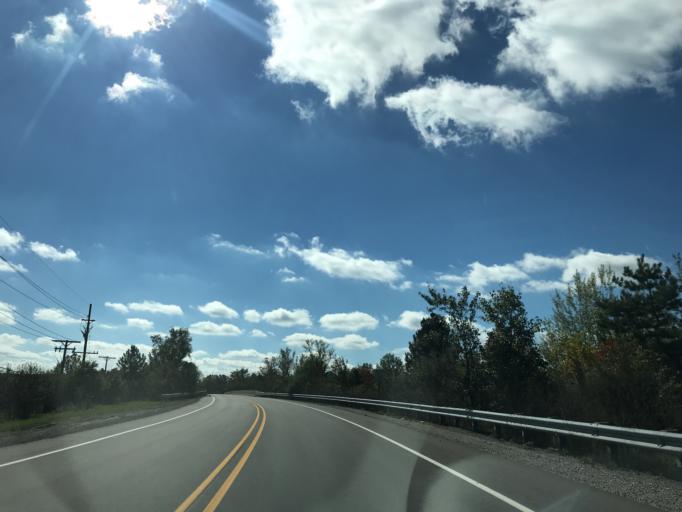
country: US
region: Michigan
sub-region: Washtenaw County
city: Ann Arbor
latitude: 42.2959
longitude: -83.6825
